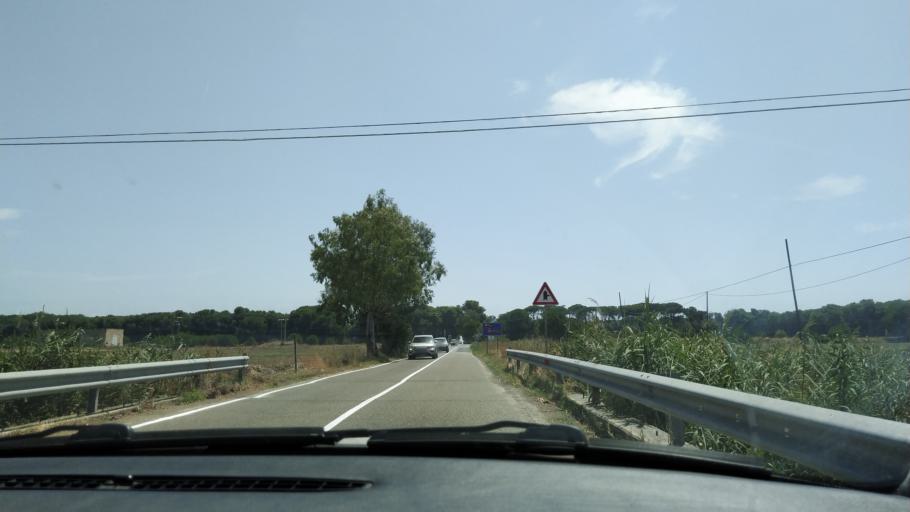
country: IT
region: Basilicate
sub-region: Provincia di Matera
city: Marconia
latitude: 40.3255
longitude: 16.7910
